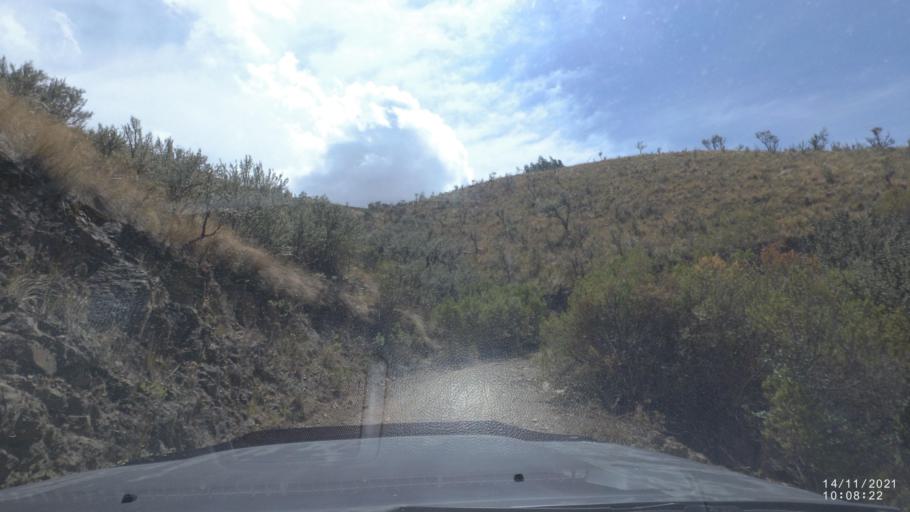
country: BO
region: Cochabamba
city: Cochabamba
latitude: -17.3468
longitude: -66.0879
